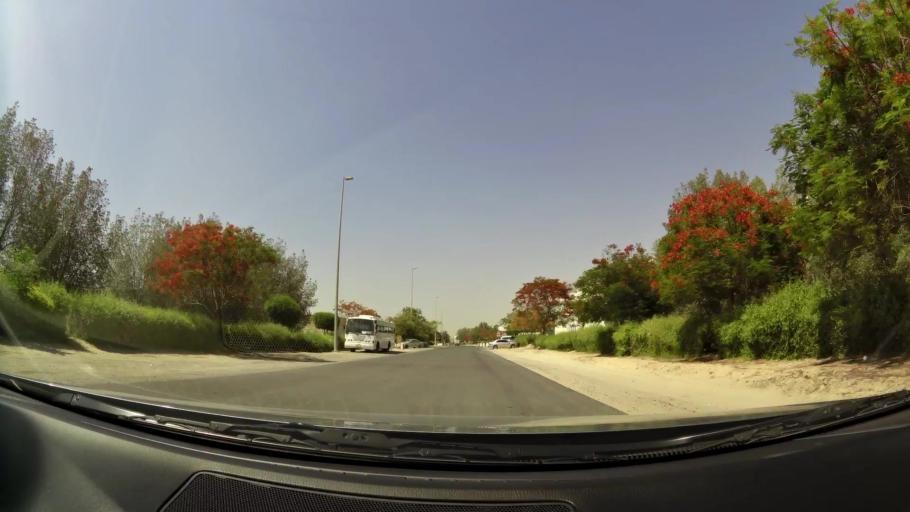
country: AE
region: Dubai
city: Dubai
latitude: 24.9804
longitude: 55.1473
